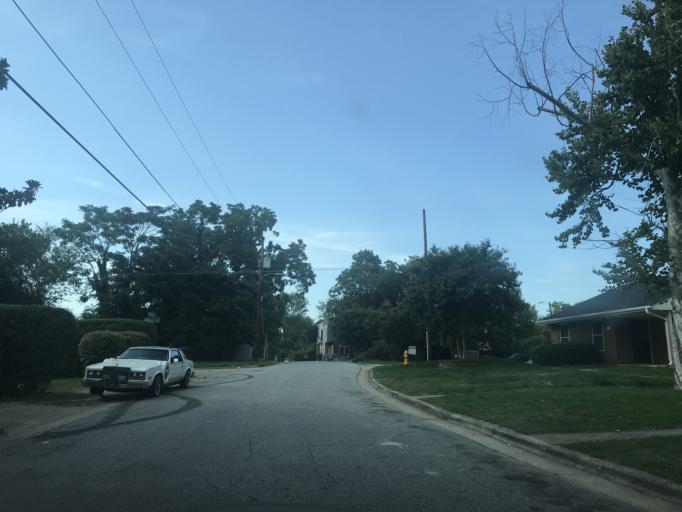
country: US
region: North Carolina
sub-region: Wake County
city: Raleigh
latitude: 35.7741
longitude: -78.6260
